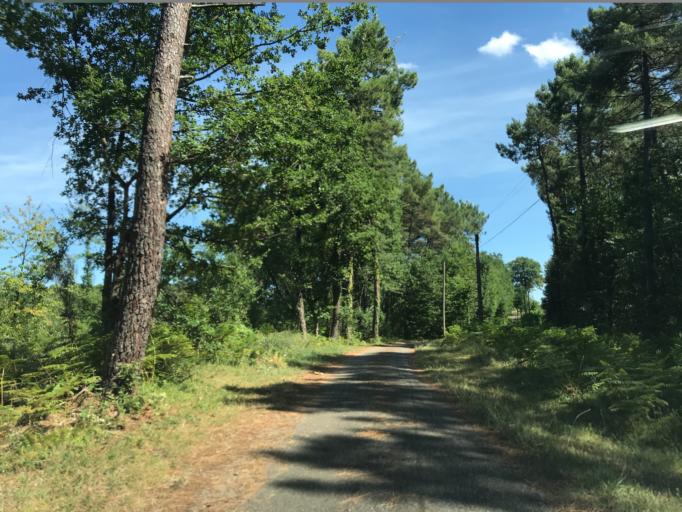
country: FR
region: Aquitaine
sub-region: Departement de la Dordogne
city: Sarlat-la-Caneda
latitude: 44.9117
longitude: 1.1758
